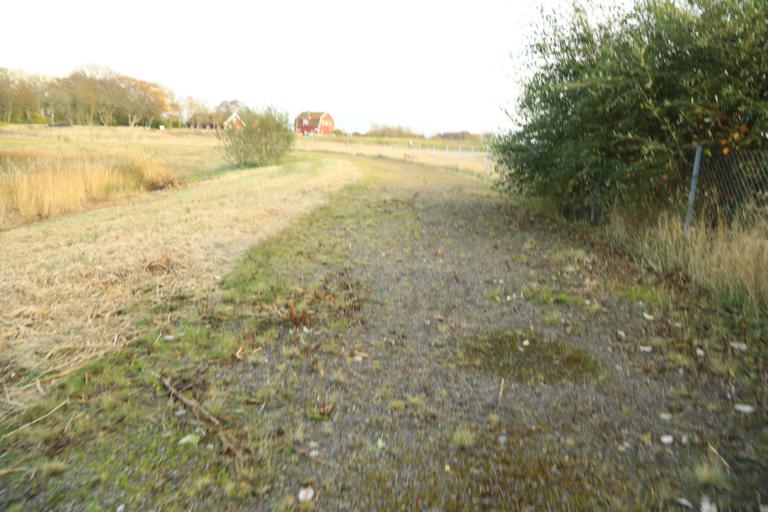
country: SE
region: Halland
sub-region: Varbergs Kommun
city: Varberg
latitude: 57.1197
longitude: 12.3063
